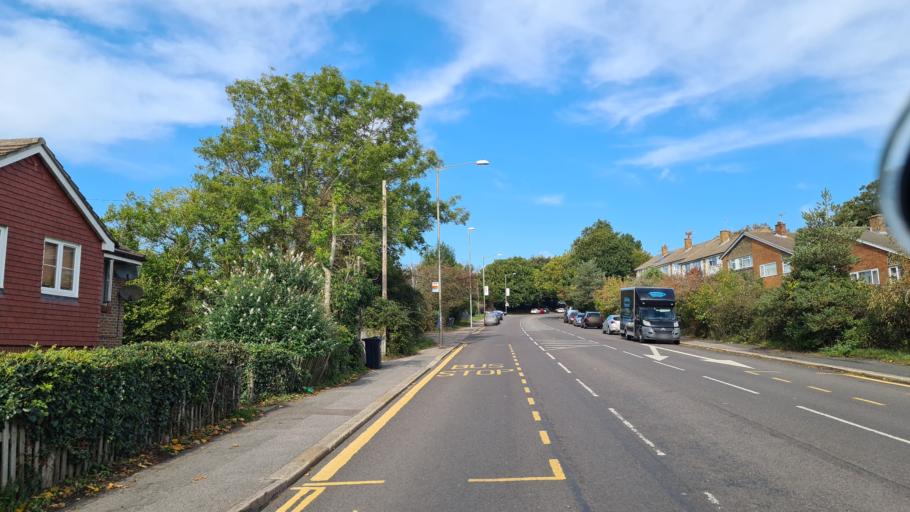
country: GB
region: England
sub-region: East Sussex
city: Saint Leonards-on-Sea
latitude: 50.8838
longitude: 0.5507
